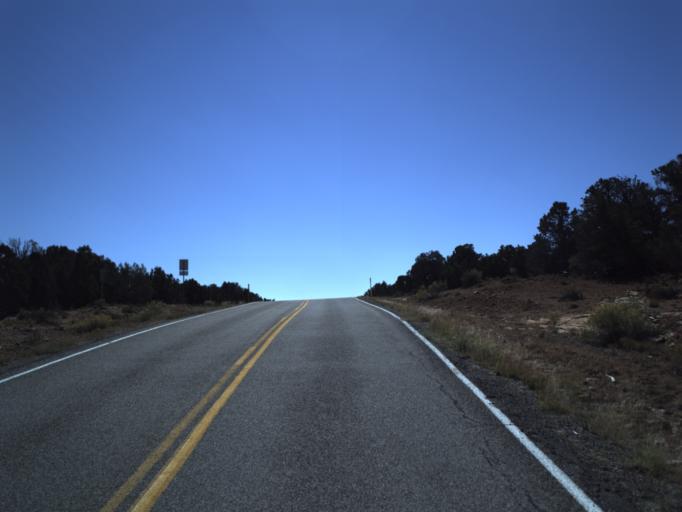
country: US
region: Utah
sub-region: San Juan County
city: Blanding
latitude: 37.5138
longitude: -109.8944
